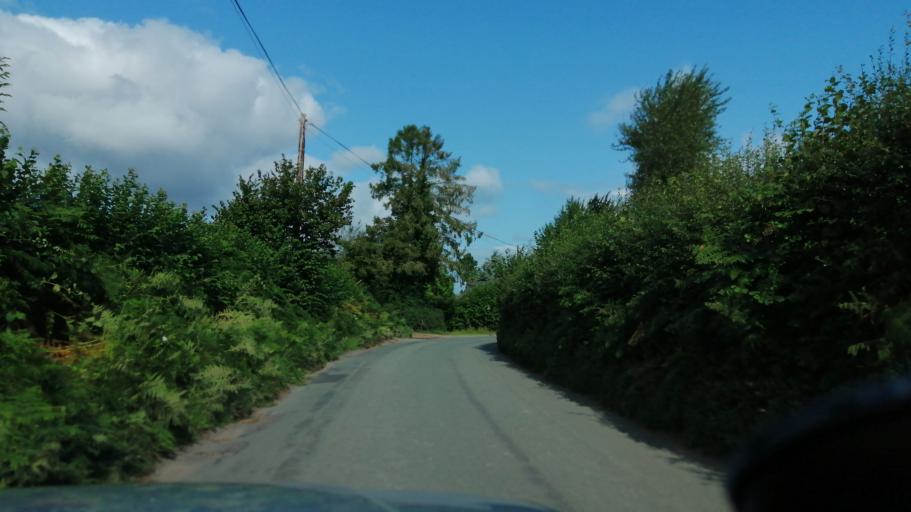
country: GB
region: England
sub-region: Herefordshire
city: Madley
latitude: 52.0590
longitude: -2.8595
